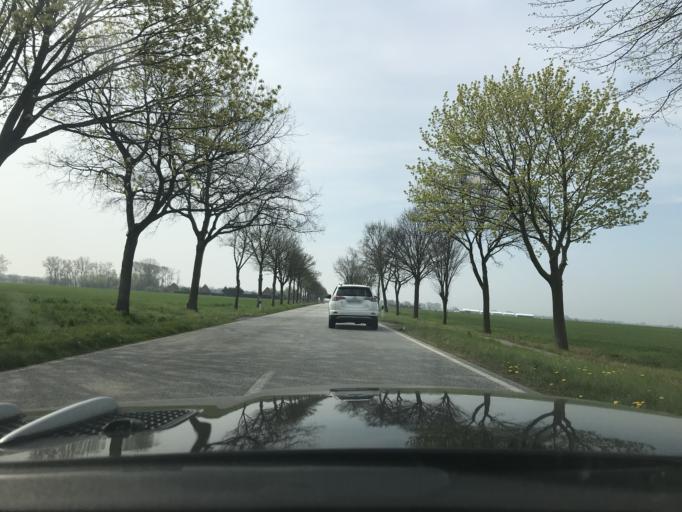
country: DE
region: Schleswig-Holstein
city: Grube
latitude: 54.2511
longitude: 11.0315
